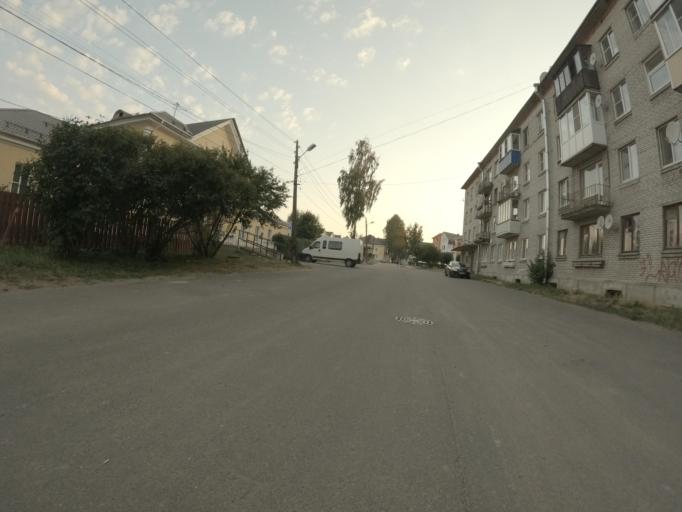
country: RU
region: Leningrad
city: Pavlovo
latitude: 59.8455
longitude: 30.9382
